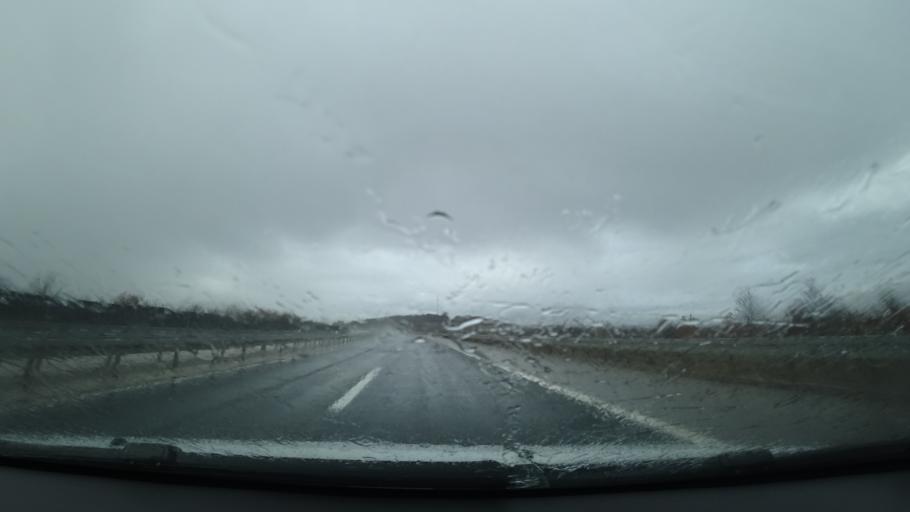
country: HR
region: Licko-Senjska
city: Gospic
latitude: 44.6499
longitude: 15.4340
